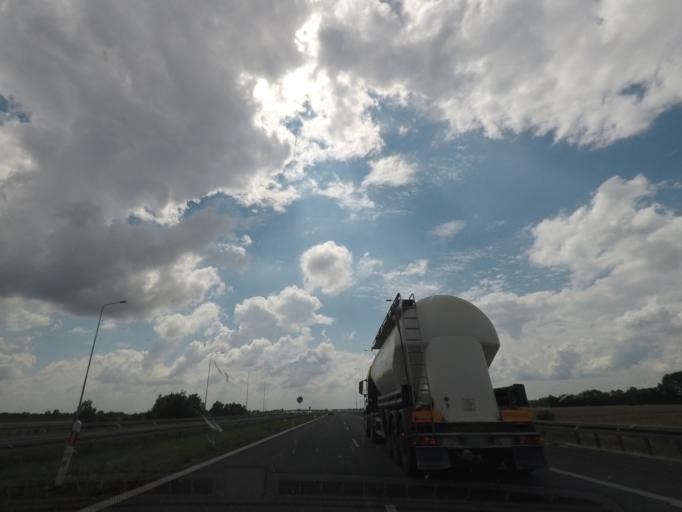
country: PL
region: Lodz Voivodeship
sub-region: Powiat leczycki
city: Piatek
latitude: 52.0019
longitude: 19.5452
